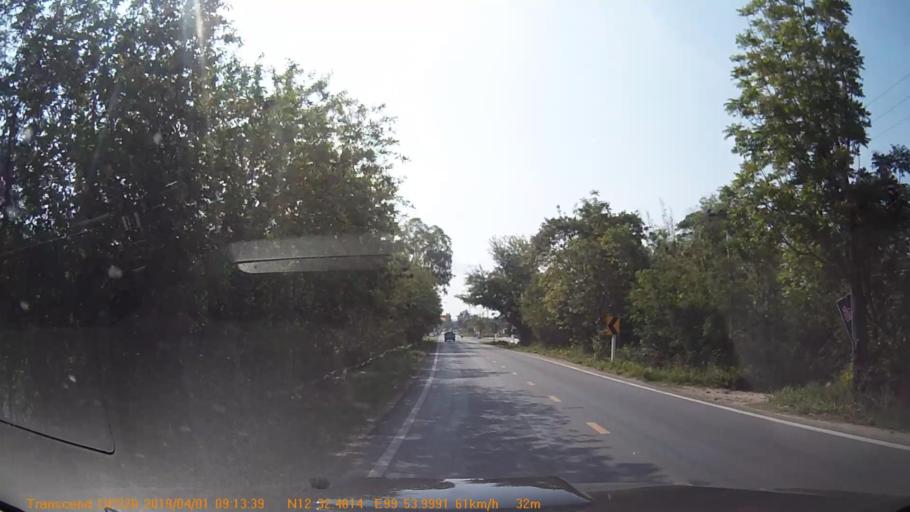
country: TH
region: Prachuap Khiri Khan
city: Hua Hin
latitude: 12.5412
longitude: 99.9002
